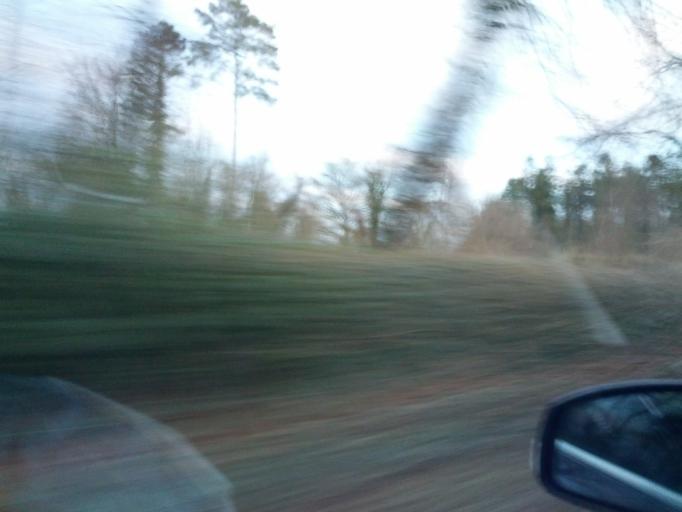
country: IE
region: Connaught
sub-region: County Galway
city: Athenry
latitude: 53.3331
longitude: -8.7695
